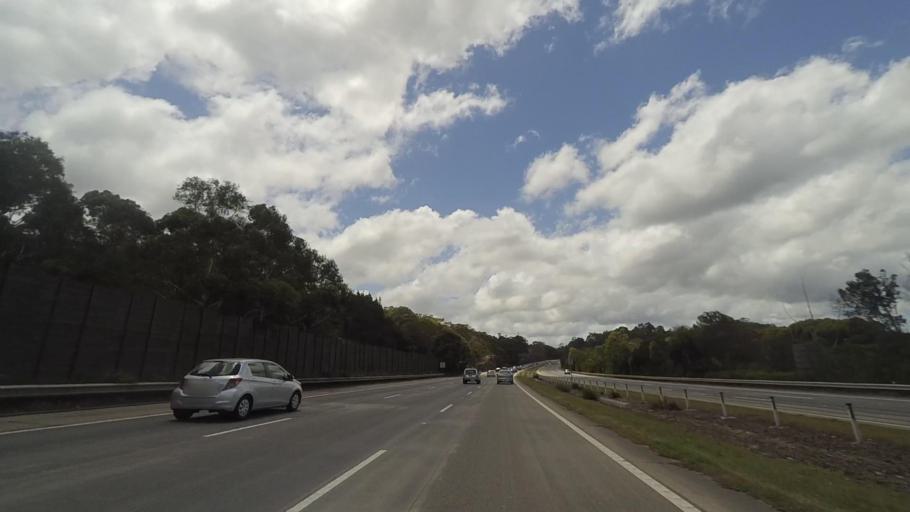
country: AU
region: New South Wales
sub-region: Hornsby Shire
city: Mount Colah
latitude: -33.6699
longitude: 151.1209
